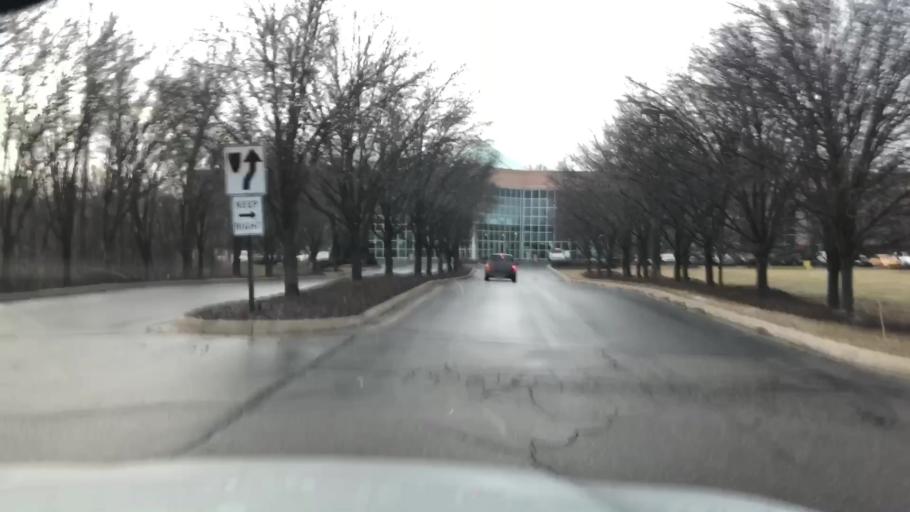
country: US
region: Michigan
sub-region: Wayne County
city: Northville
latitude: 42.4489
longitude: -83.4359
